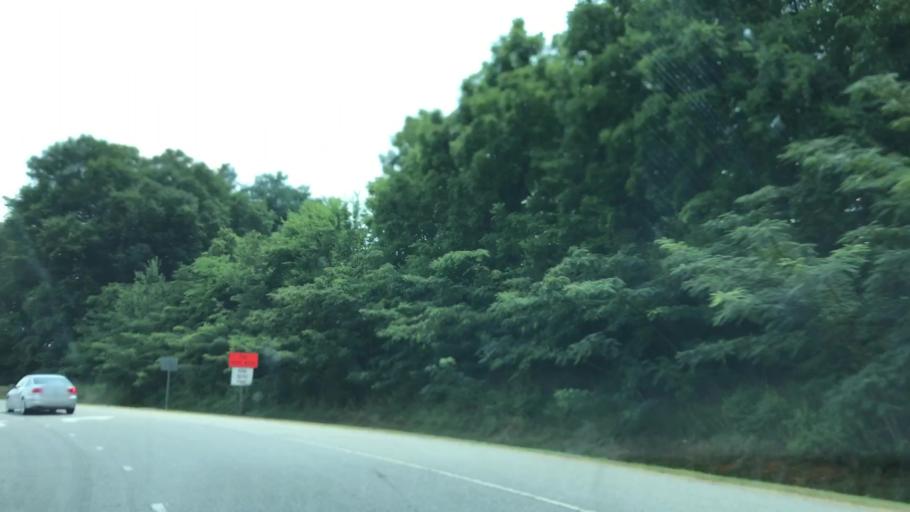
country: US
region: North Carolina
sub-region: Gaston County
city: Davidson
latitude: 35.5307
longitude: -80.8644
